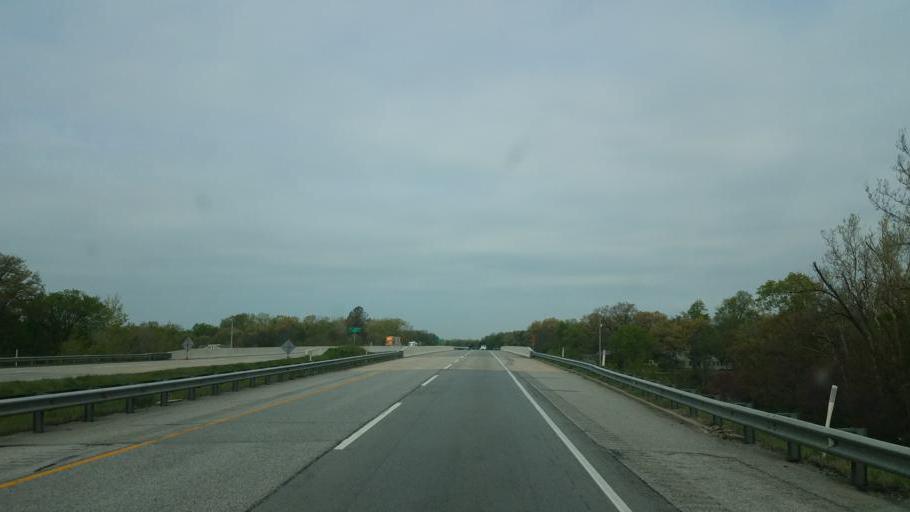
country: US
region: Indiana
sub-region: Elkhart County
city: Bristol
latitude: 41.7350
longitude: -85.8090
